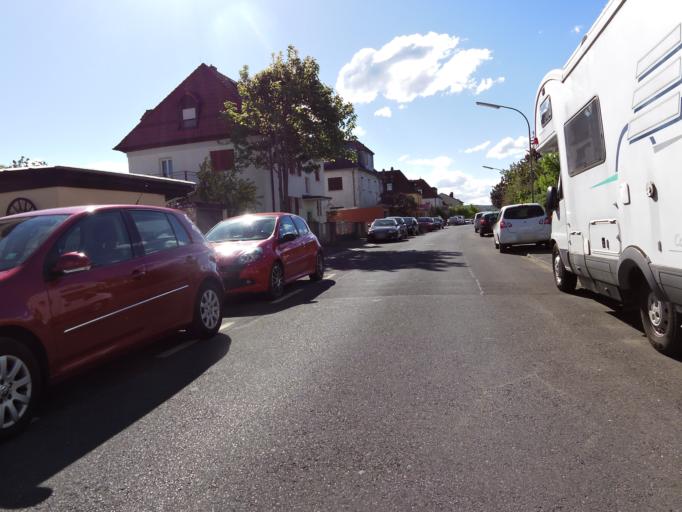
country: DE
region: Bavaria
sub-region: Regierungsbezirk Unterfranken
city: Wuerzburg
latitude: 49.7850
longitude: 9.9439
